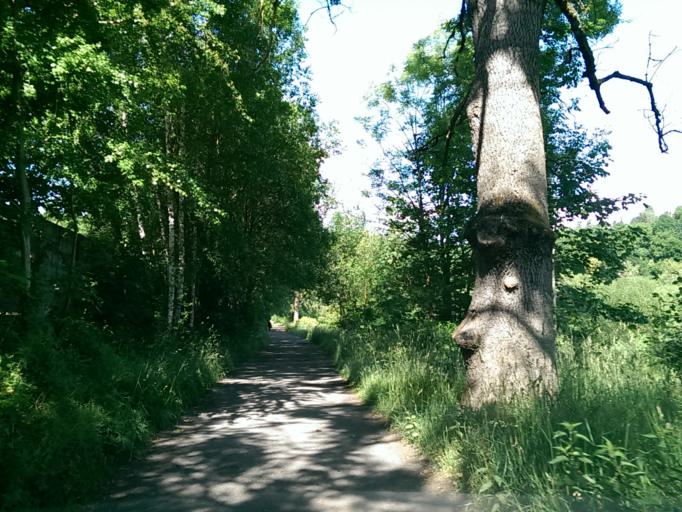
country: CZ
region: Liberecky
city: Semily
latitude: 50.6137
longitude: 15.3203
